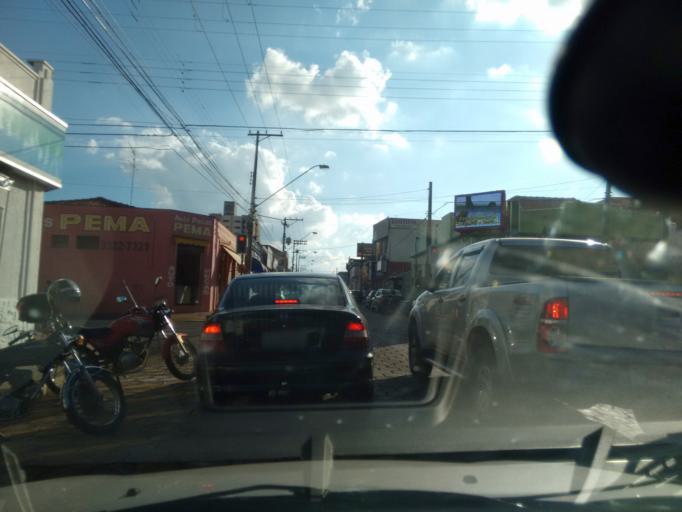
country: BR
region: Sao Paulo
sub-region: Araraquara
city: Araraquara
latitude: -21.7987
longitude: -48.1783
